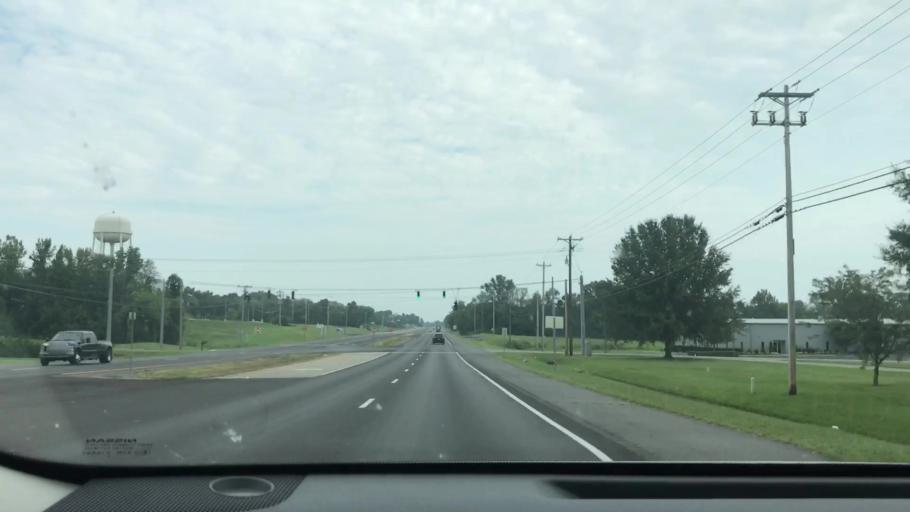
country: US
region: Kentucky
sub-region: Calloway County
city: Murray
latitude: 36.6579
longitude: -88.3057
